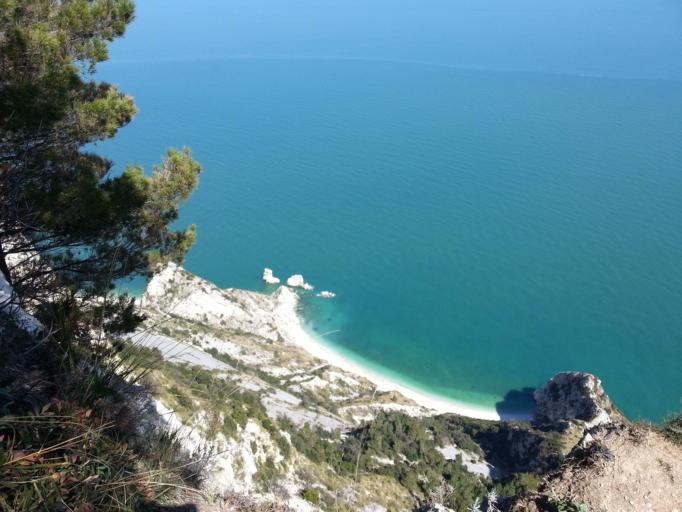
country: IT
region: The Marches
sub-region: Provincia di Ancona
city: Sirolo
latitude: 43.5439
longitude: 13.6233
